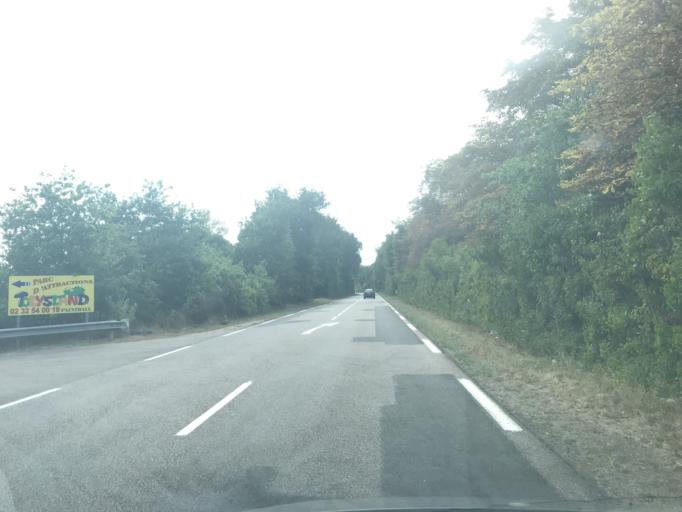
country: FR
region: Haute-Normandie
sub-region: Departement de l'Eure
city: Les Andelys
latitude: 49.2324
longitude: 1.3787
